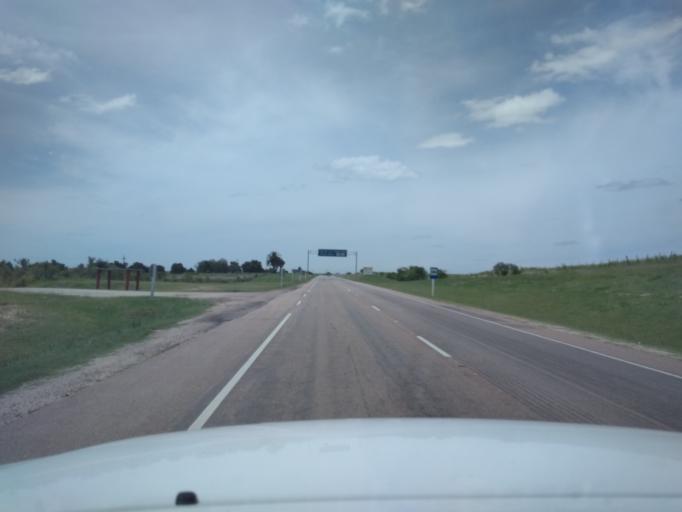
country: UY
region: Florida
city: Cardal
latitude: -34.3229
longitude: -56.2432
